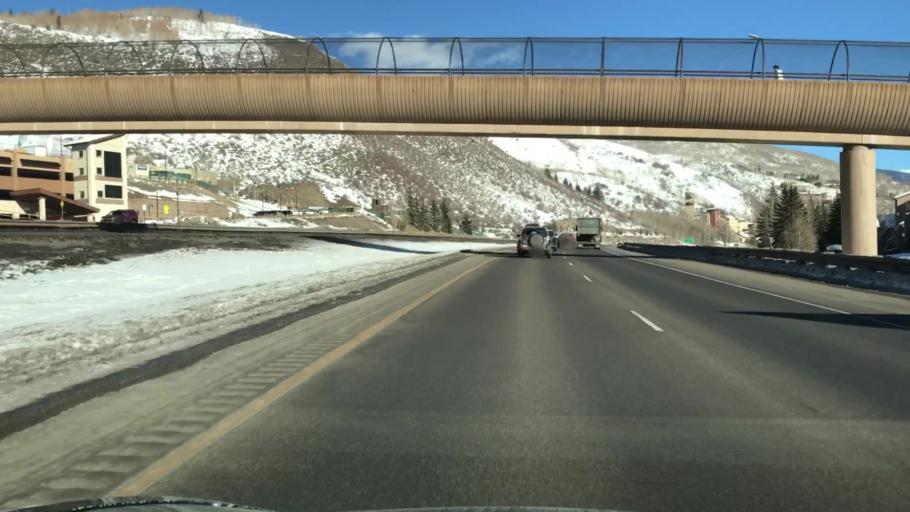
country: US
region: Colorado
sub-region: Eagle County
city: Vail
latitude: 39.6450
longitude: -106.3906
